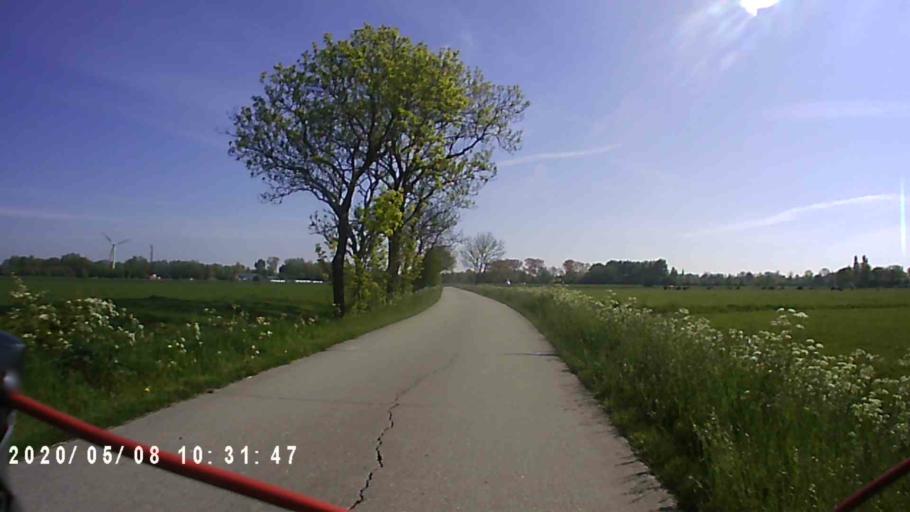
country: NL
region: Groningen
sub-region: Gemeente Winsum
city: Winsum
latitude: 53.3288
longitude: 6.4999
